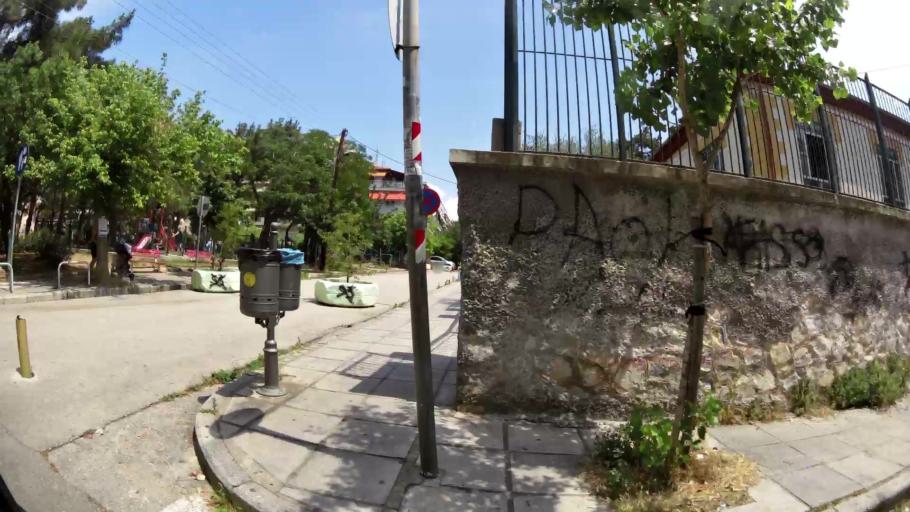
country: GR
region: Central Macedonia
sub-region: Nomos Thessalonikis
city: Triandria
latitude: 40.6178
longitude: 22.9759
